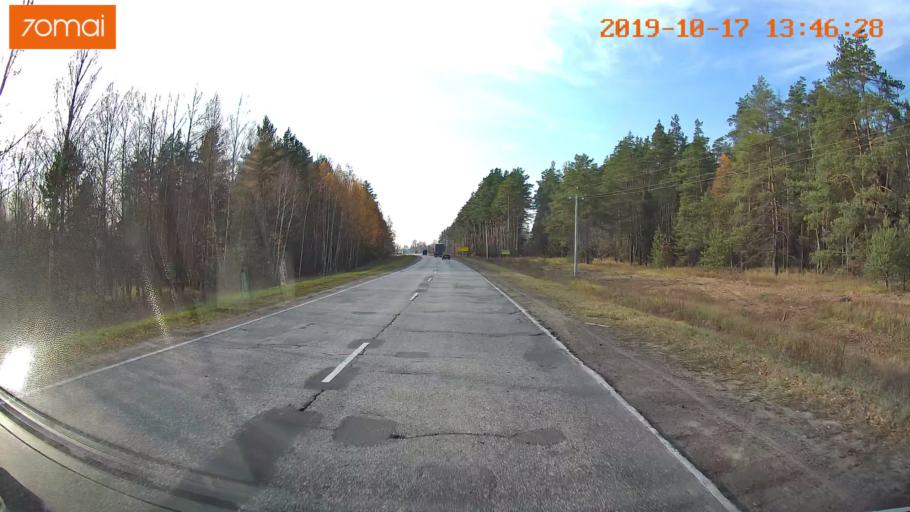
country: RU
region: Rjazan
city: Tuma
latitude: 55.1476
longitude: 40.4885
